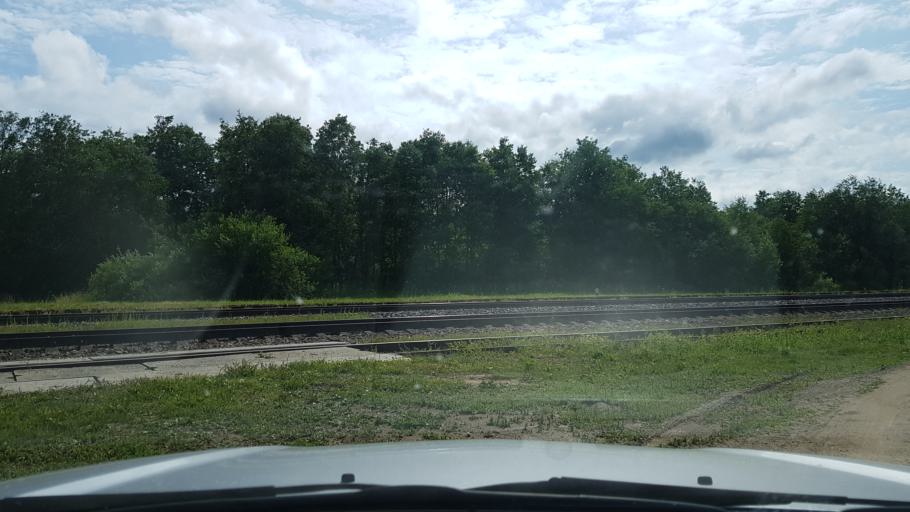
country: EE
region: Ida-Virumaa
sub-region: Narva-Joesuu linn
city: Narva-Joesuu
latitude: 59.3635
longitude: 27.9217
